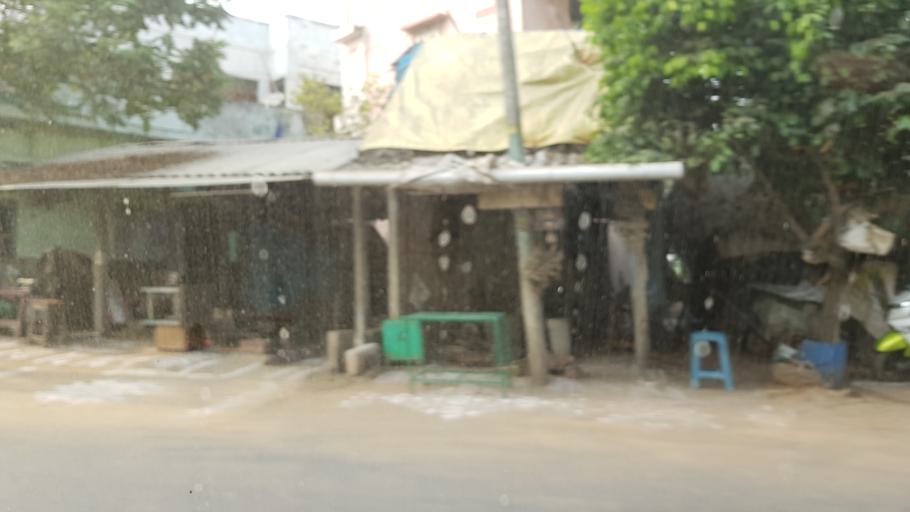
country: IN
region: Andhra Pradesh
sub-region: West Godavari
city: Akividu
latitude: 16.5315
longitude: 81.3910
